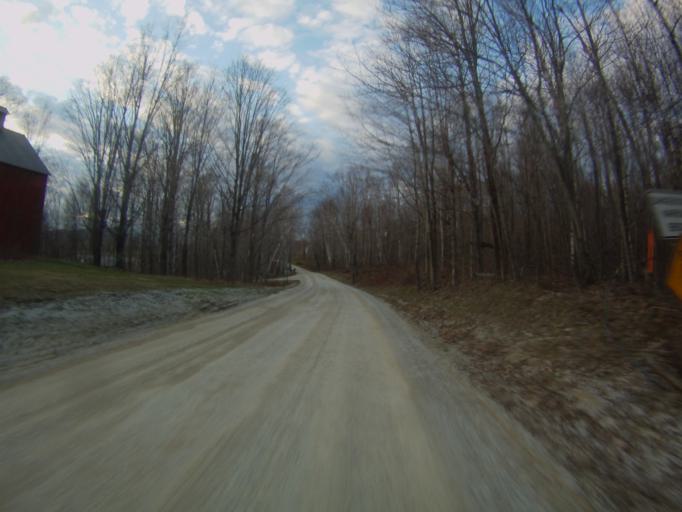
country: US
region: Vermont
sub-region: Rutland County
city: Brandon
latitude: 43.8878
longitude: -73.0099
